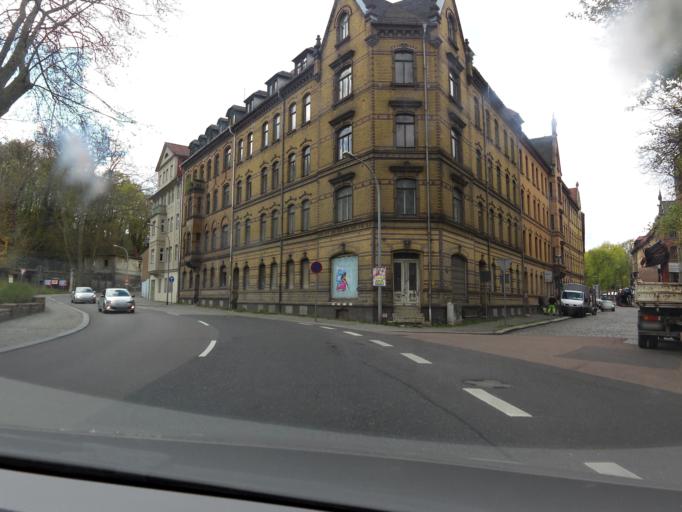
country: DE
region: Saxony-Anhalt
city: Weissenfels
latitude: 51.1985
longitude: 11.9629
